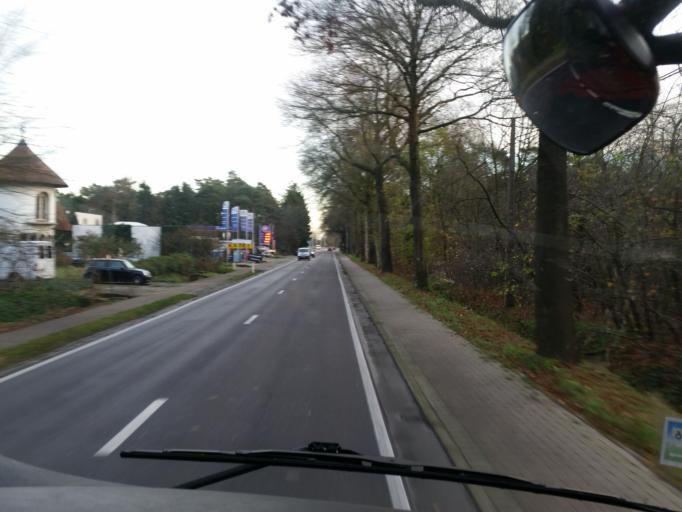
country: BE
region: Flanders
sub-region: Provincie Antwerpen
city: Oud-Turnhout
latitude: 51.3003
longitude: 5.0236
